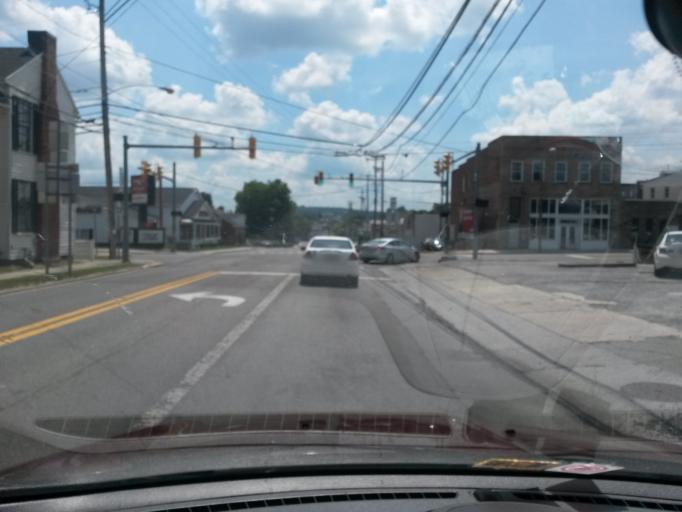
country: US
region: West Virginia
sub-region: Mercer County
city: Princeton
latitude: 37.3671
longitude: -81.1028
